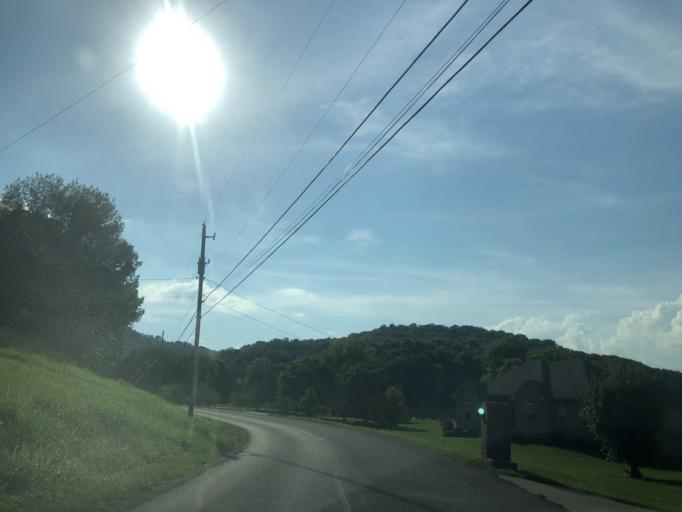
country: US
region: Tennessee
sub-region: Davidson County
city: Nashville
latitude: 36.2389
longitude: -86.8359
